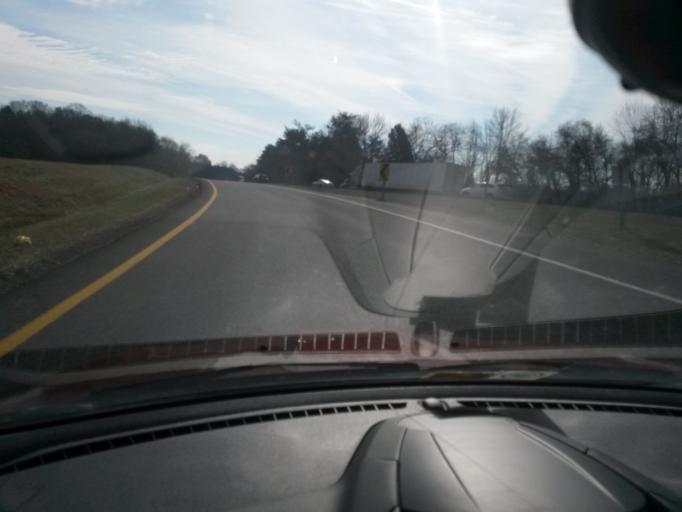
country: US
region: Virginia
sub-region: Roanoke County
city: Hollins
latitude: 37.3390
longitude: -79.9975
